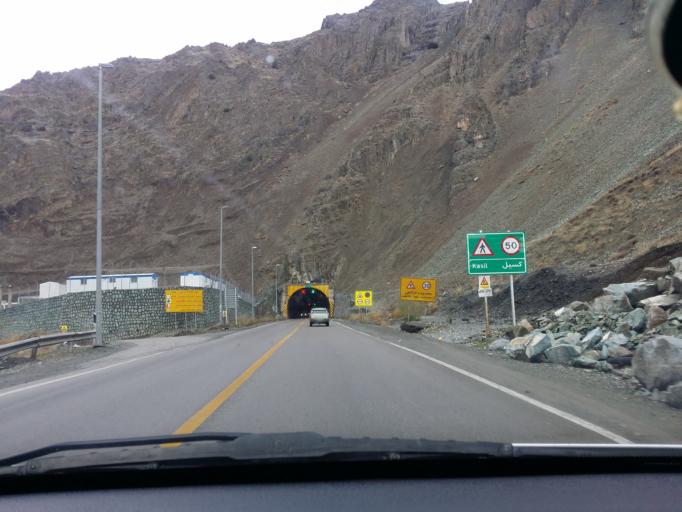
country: IR
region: Tehran
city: Tajrish
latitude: 36.0216
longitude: 51.3018
